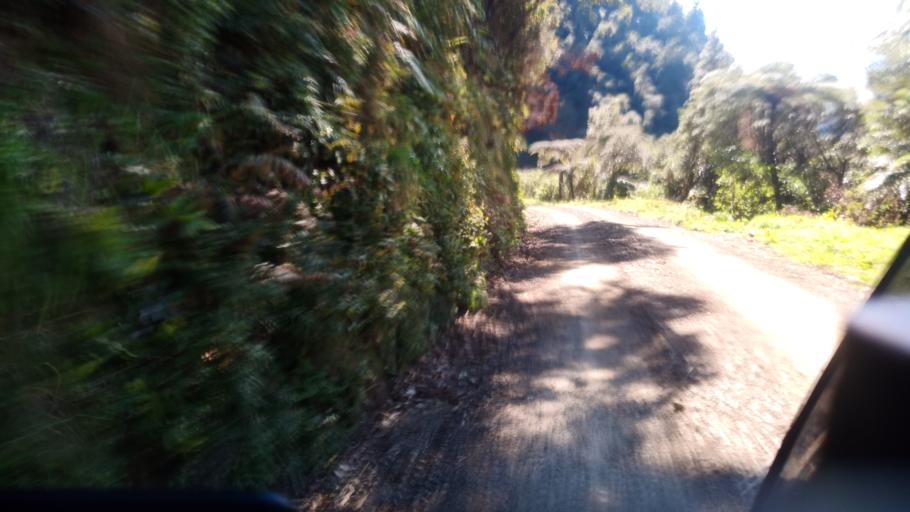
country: NZ
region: Bay of Plenty
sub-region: Opotiki District
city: Opotiki
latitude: -38.0872
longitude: 177.4781
